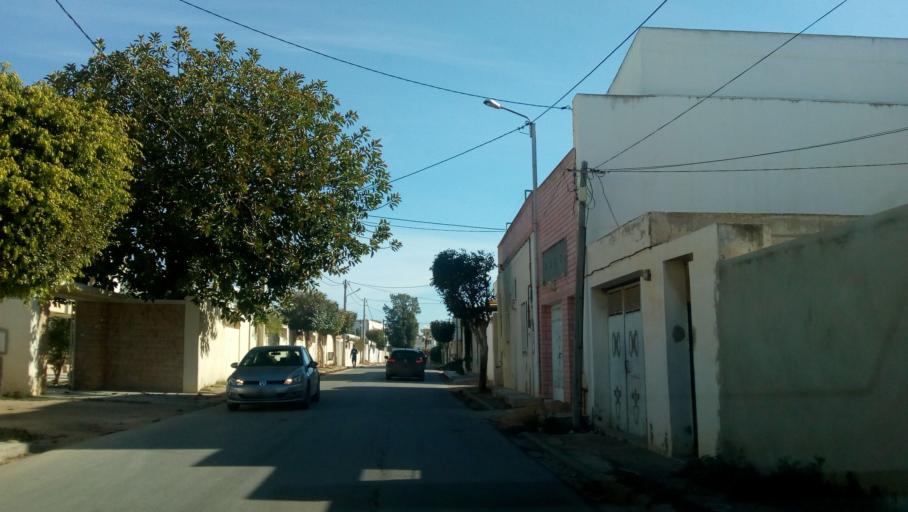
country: TN
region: Safaqis
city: Sfax
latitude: 34.7487
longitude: 10.7376
